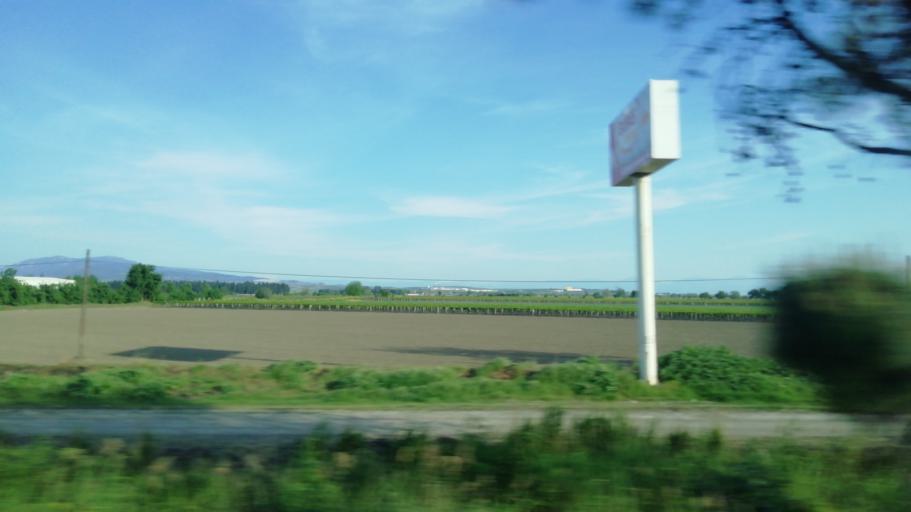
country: TR
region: Manisa
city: Saruhanli
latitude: 38.7259
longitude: 27.5725
